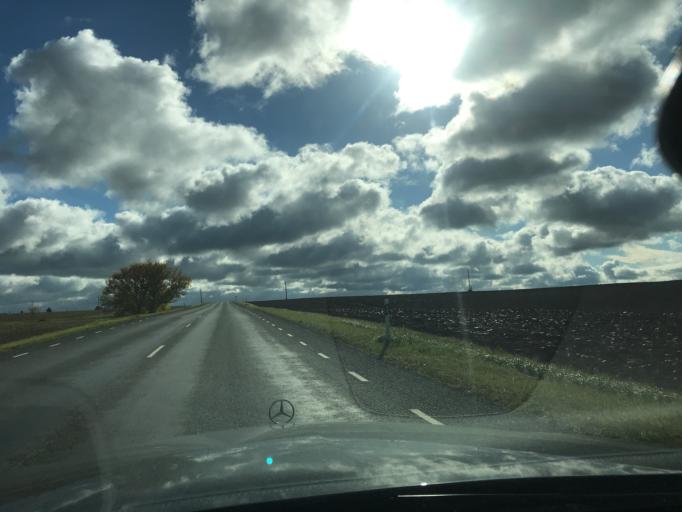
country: EE
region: Vorumaa
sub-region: Antsla vald
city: Vana-Antsla
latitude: 57.9206
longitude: 26.3471
